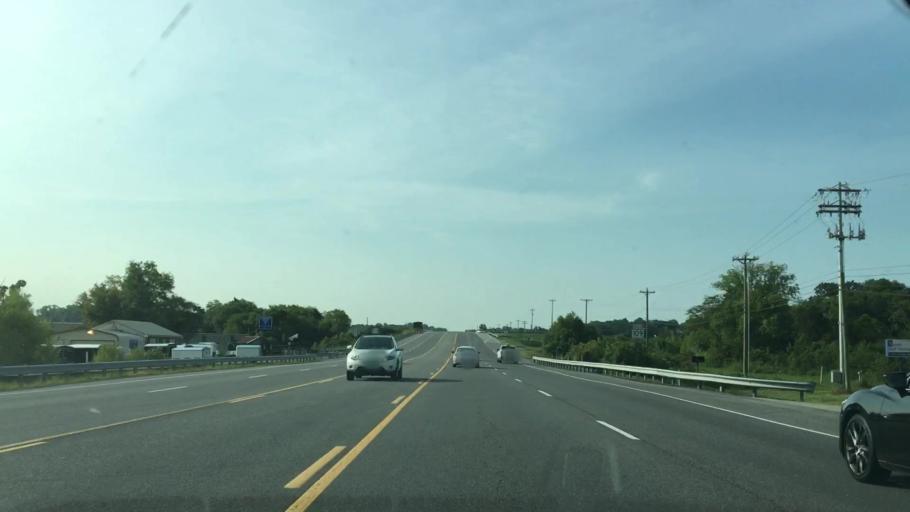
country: US
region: Tennessee
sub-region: Wilson County
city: Mount Juliet
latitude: 36.2304
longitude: -86.4282
